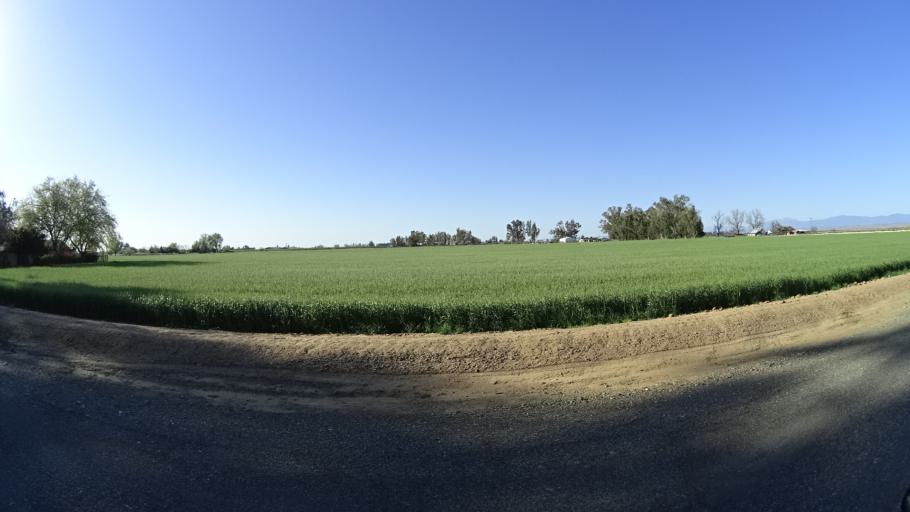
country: US
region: California
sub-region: Glenn County
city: Orland
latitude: 39.7588
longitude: -122.2457
